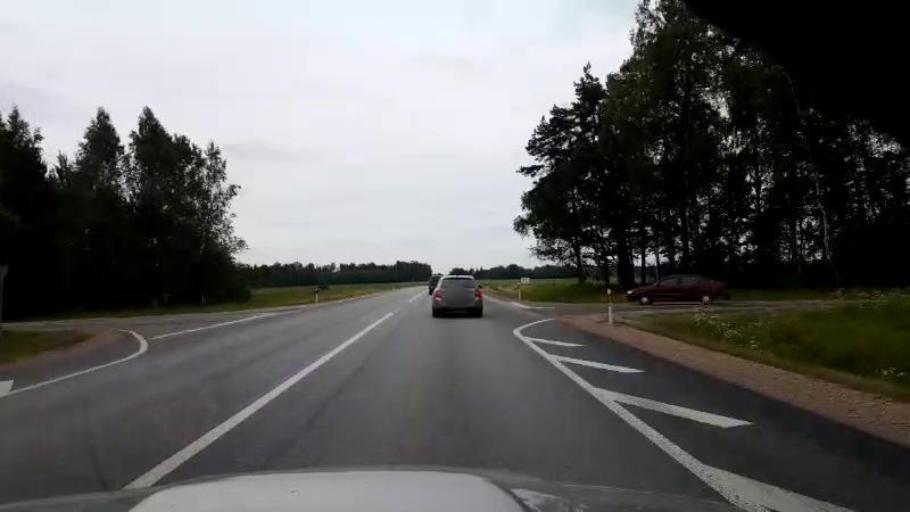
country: LV
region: Lecava
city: Iecava
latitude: 56.6508
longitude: 24.2293
